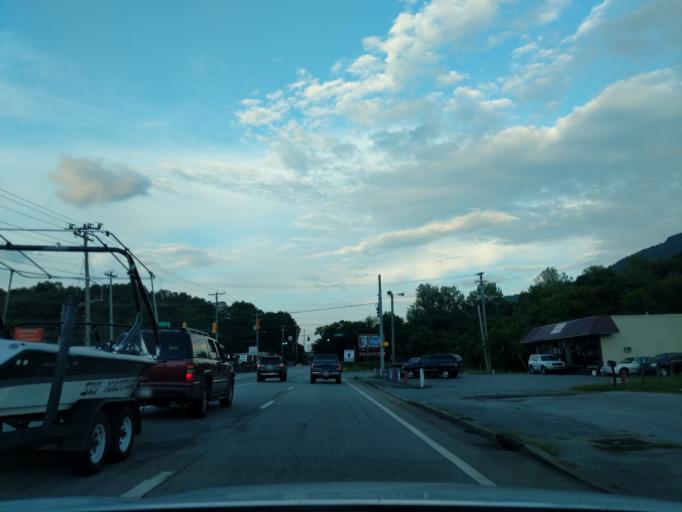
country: US
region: Tennessee
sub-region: Hamilton County
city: Lookout Mountain
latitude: 35.0201
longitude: -85.3667
